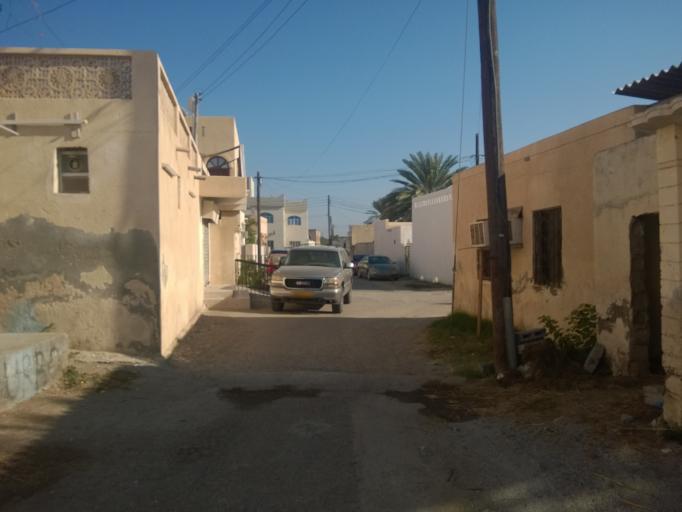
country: OM
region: Muhafazat Masqat
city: As Sib al Jadidah
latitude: 23.6681
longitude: 58.1873
